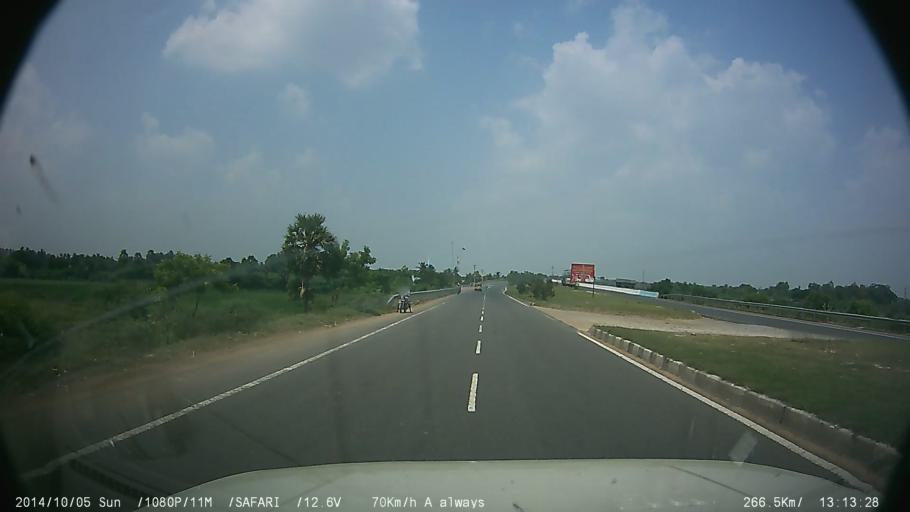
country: IN
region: Tamil Nadu
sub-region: Villupuram
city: Villupuram
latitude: 11.9678
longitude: 79.5008
